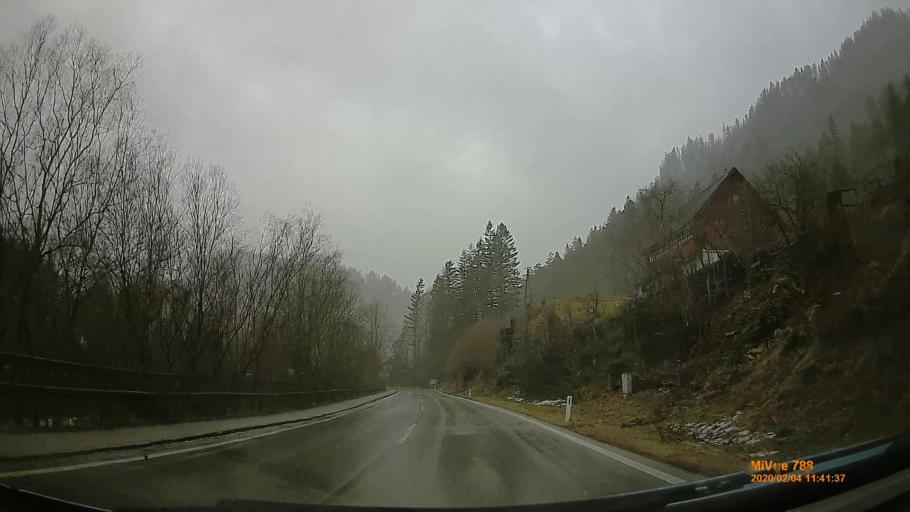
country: AT
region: Styria
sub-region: Politischer Bezirk Bruck-Muerzzuschlag
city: Muerzsteg
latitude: 47.6740
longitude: 15.4994
